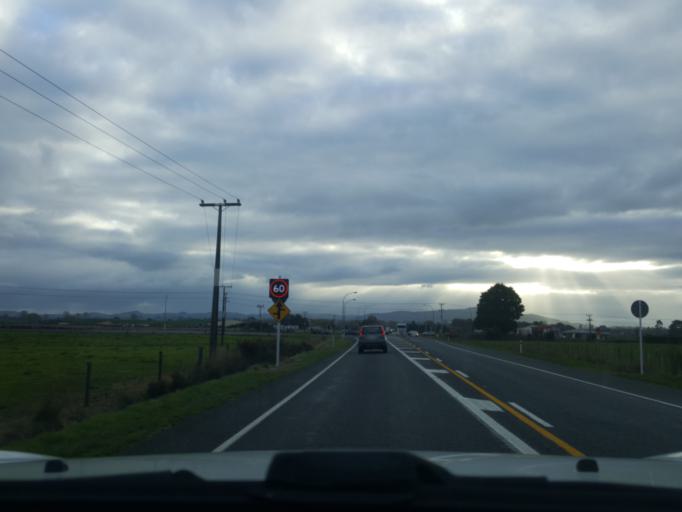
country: NZ
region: Waikato
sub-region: Matamata-Piako District
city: Matamata
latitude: -37.8893
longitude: 175.7779
